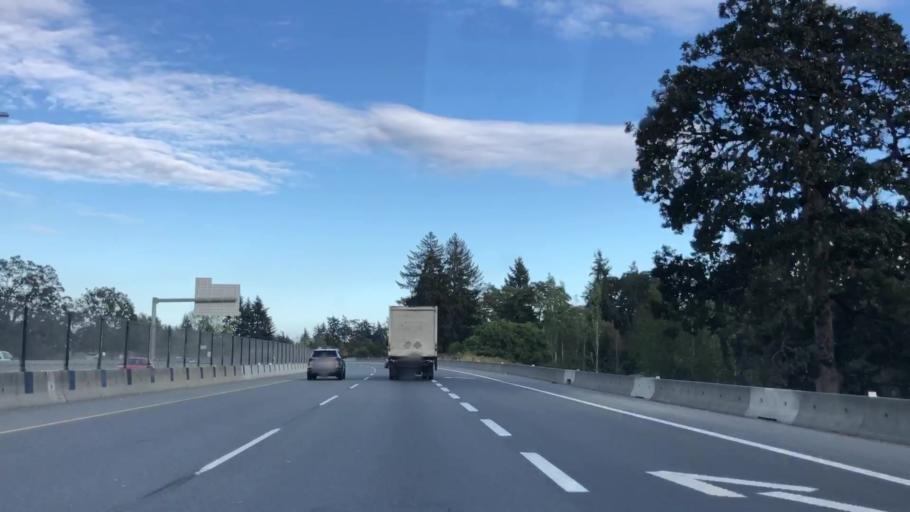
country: CA
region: British Columbia
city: Langford
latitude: 48.4533
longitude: -123.5138
